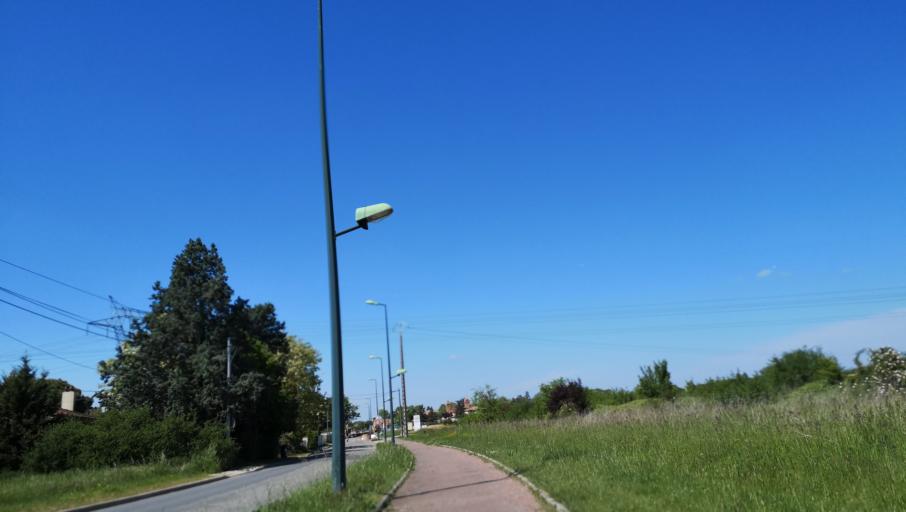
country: FR
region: Midi-Pyrenees
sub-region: Departement de la Haute-Garonne
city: Beauzelle
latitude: 43.6743
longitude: 1.3681
